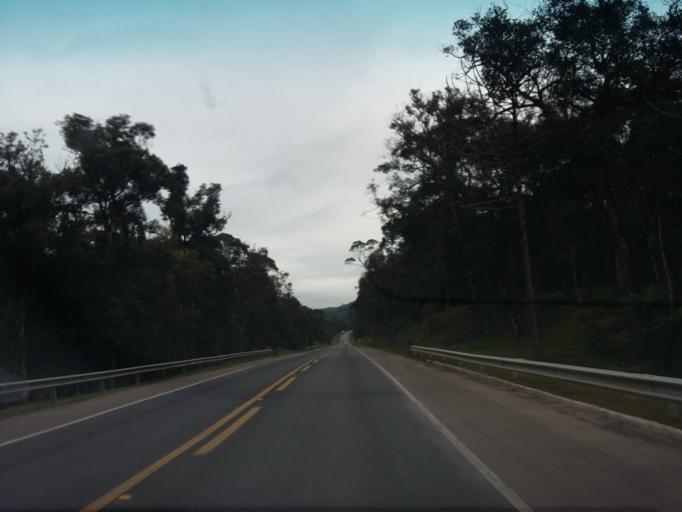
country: BR
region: Santa Catarina
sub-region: Santa Cecilia
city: Santa Cecilia
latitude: -26.7254
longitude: -50.3105
